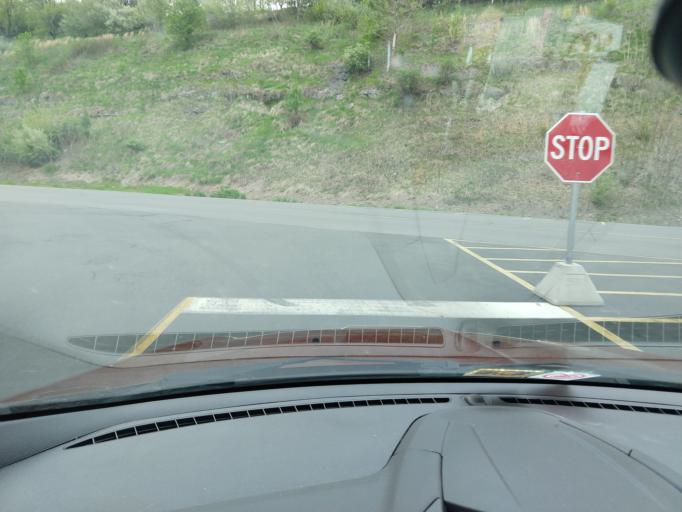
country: US
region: West Virginia
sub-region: Harrison County
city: Bridgeport
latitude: 39.3140
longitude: -80.2694
